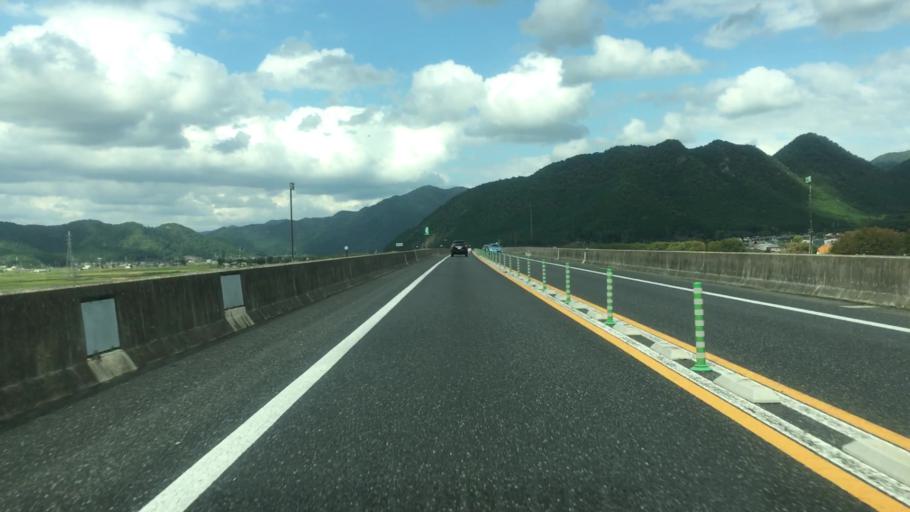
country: JP
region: Kyoto
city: Fukuchiyama
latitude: 35.1972
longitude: 135.0425
